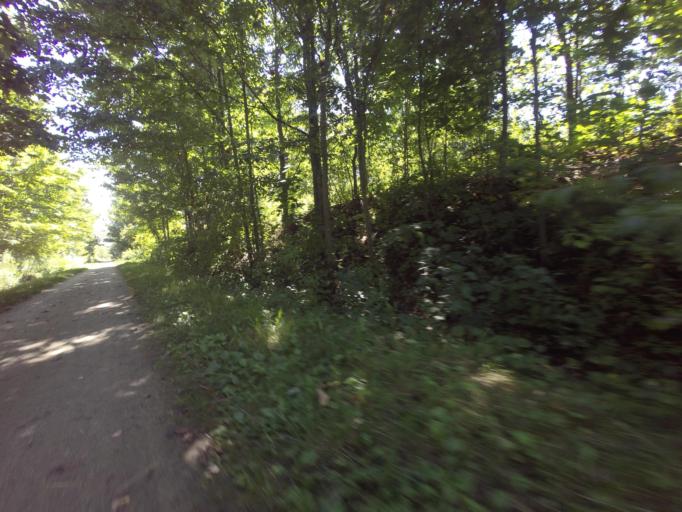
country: CA
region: Ontario
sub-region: Wellington County
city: Guelph
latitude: 43.7393
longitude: -80.3550
